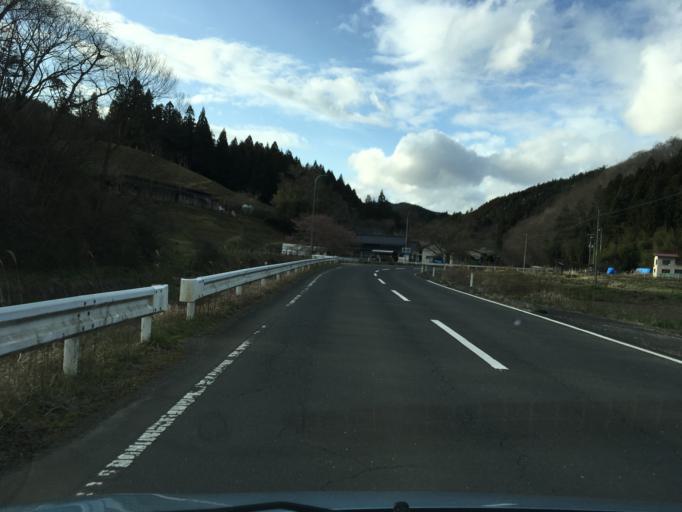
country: JP
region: Iwate
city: Ichinoseki
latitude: 38.7998
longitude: 141.3179
